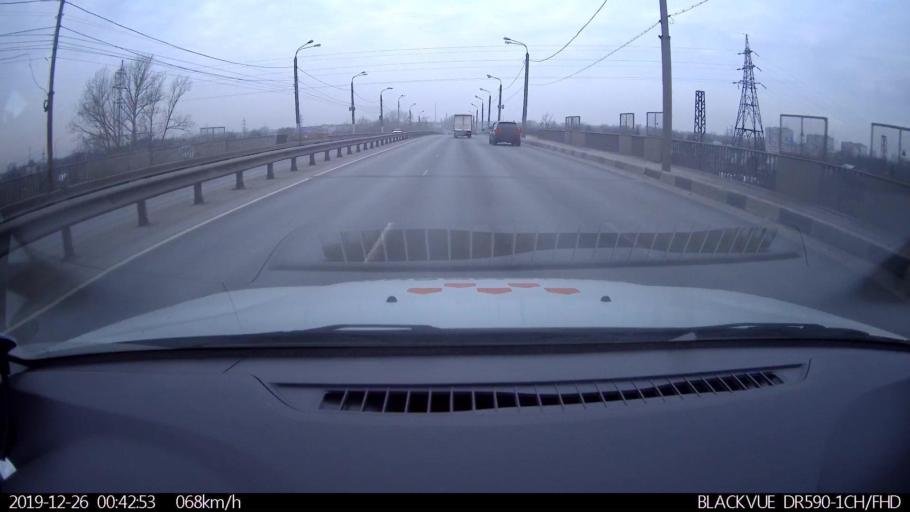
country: RU
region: Nizjnij Novgorod
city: Nizhniy Novgorod
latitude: 56.2964
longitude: 43.8790
